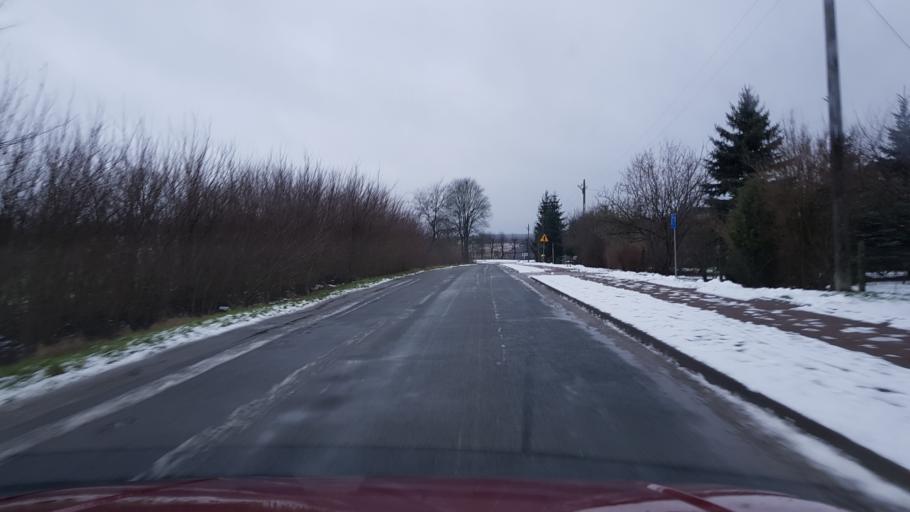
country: PL
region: West Pomeranian Voivodeship
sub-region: Powiat goleniowski
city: Osina
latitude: 53.6026
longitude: 15.0156
